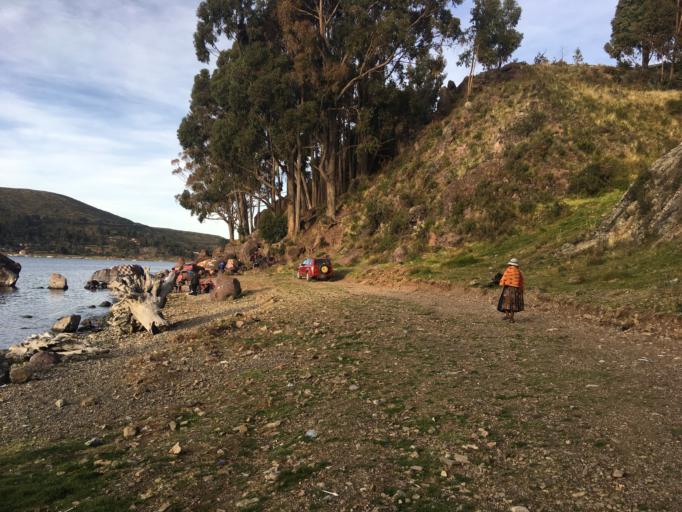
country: BO
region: La Paz
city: San Pedro
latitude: -16.2248
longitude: -68.8494
